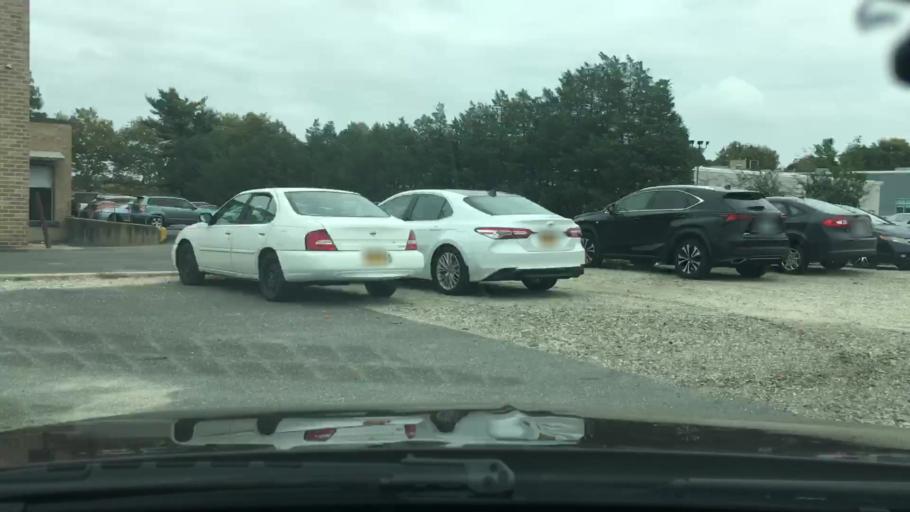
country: US
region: New York
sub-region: Suffolk County
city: Brentwood
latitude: 40.8167
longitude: -73.2489
